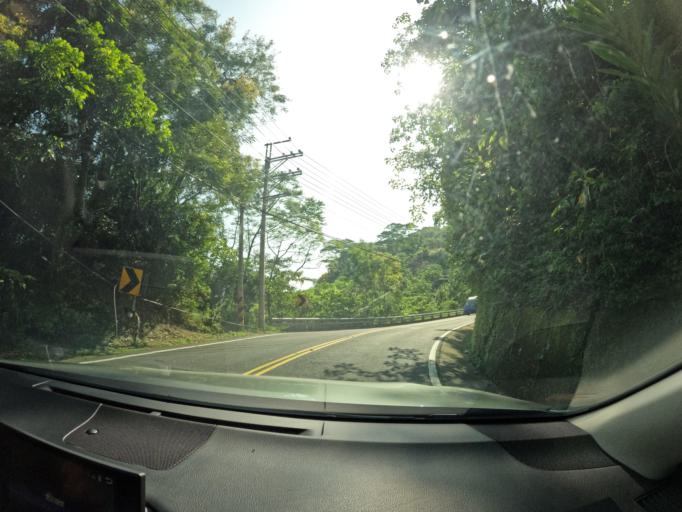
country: TW
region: Taiwan
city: Yujing
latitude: 23.0781
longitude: 120.6181
